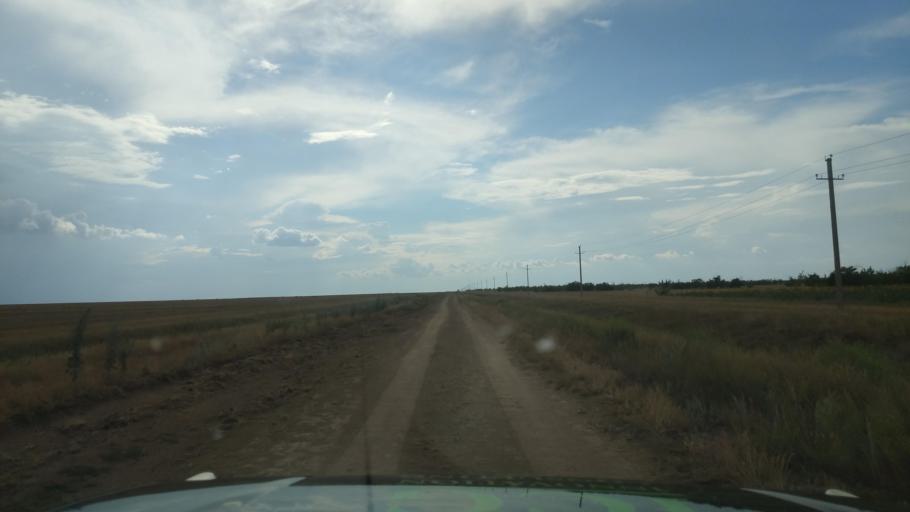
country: KZ
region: Pavlodar
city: Pavlodar
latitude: 52.5125
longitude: 77.5131
